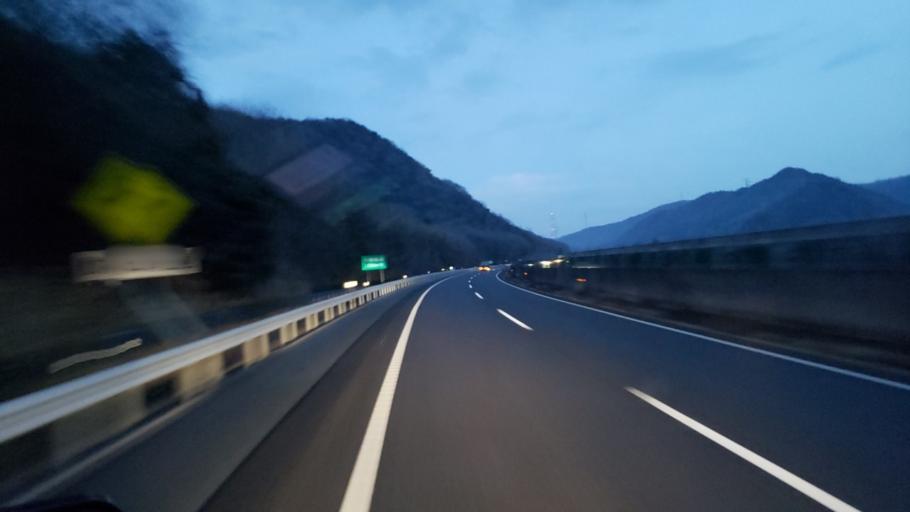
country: JP
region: Hyogo
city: Himeji
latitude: 34.8543
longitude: 134.7848
